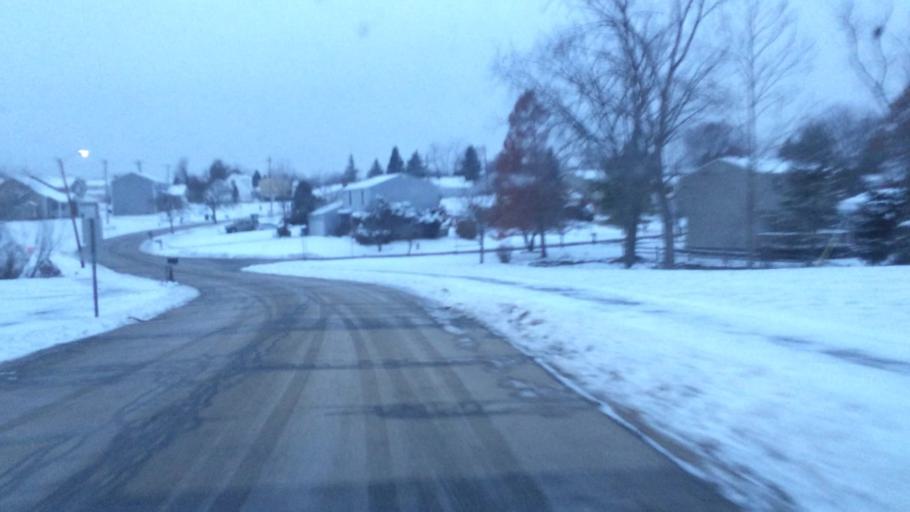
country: US
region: Ohio
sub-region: Cuyahoga County
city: Oakwood
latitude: 41.3739
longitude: -81.4963
